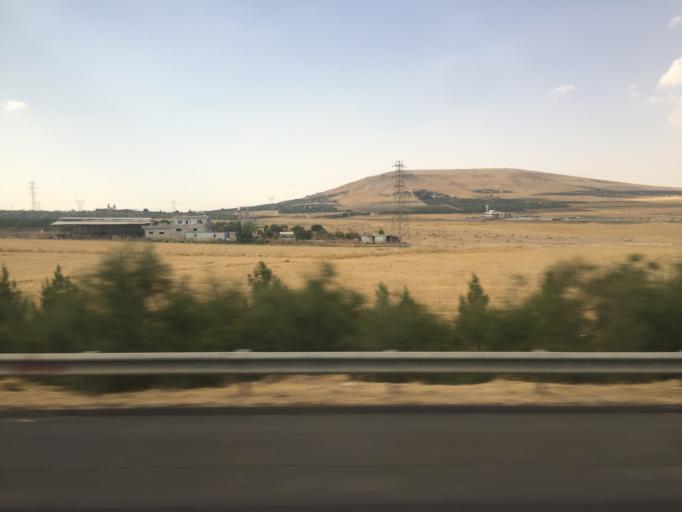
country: TR
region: Sanliurfa
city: Akziyaret
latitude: 37.2632
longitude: 38.7618
